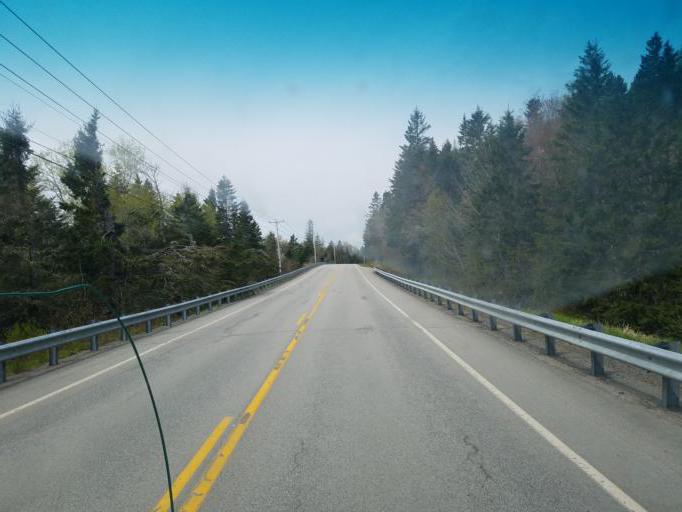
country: US
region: Maine
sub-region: Washington County
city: Eastport
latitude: 44.8014
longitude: -67.1222
